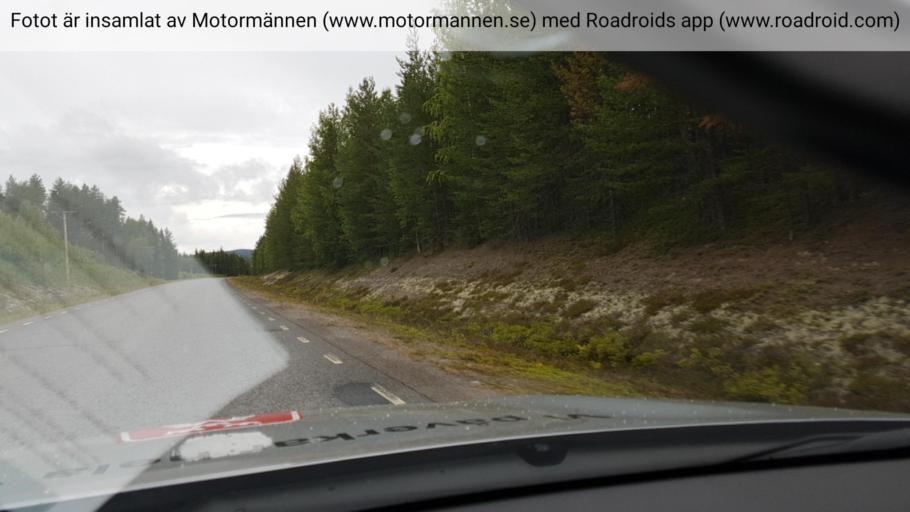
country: SE
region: Norrbotten
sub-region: Bodens Kommun
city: Boden
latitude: 65.8488
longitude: 21.4591
